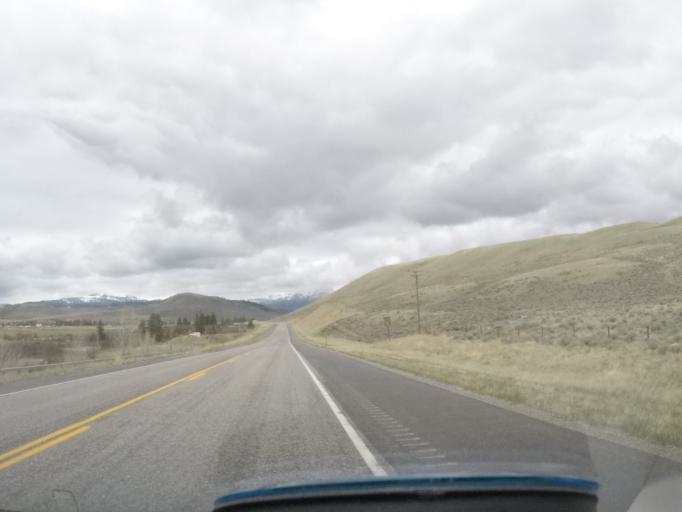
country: US
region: Wyoming
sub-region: Sublette County
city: Pinedale
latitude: 43.5896
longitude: -109.7729
